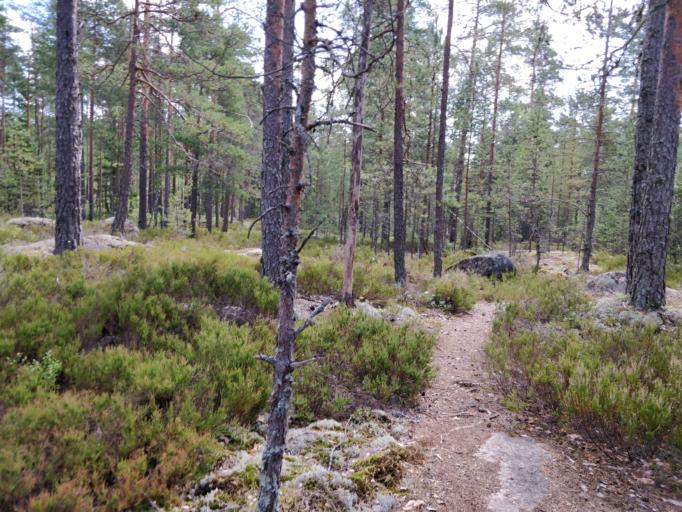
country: FI
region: Uusimaa
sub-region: Helsinki
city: Vihti
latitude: 60.3117
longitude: 24.4732
